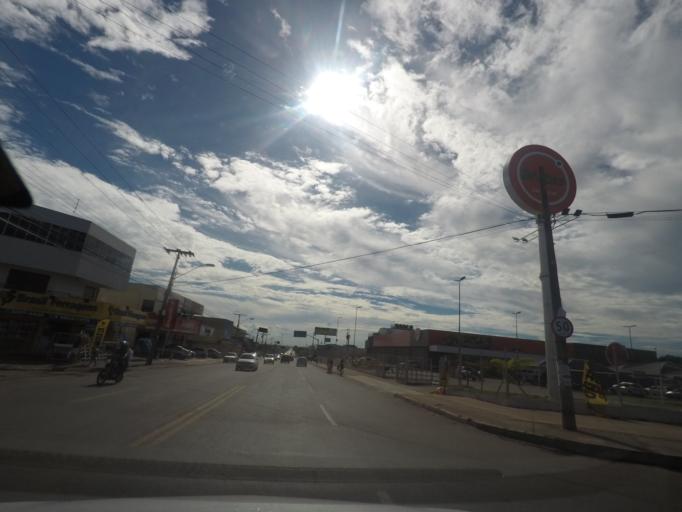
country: BR
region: Goias
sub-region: Aparecida De Goiania
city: Aparecida de Goiania
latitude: -16.8237
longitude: -49.2795
